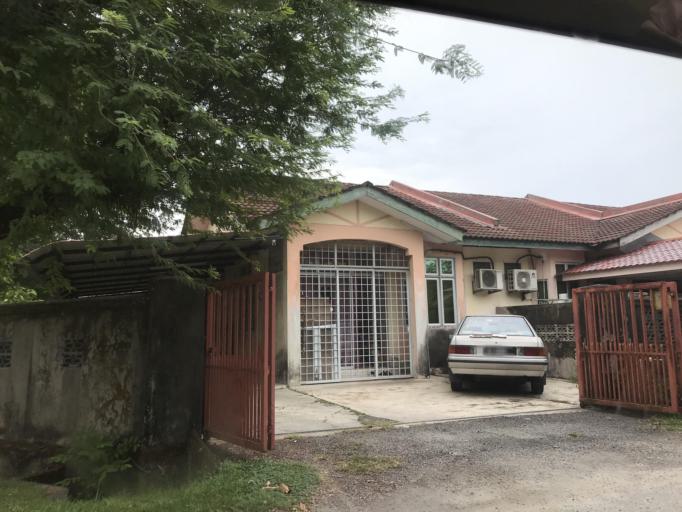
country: MY
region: Kelantan
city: Kota Bharu
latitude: 6.1155
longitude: 102.2091
